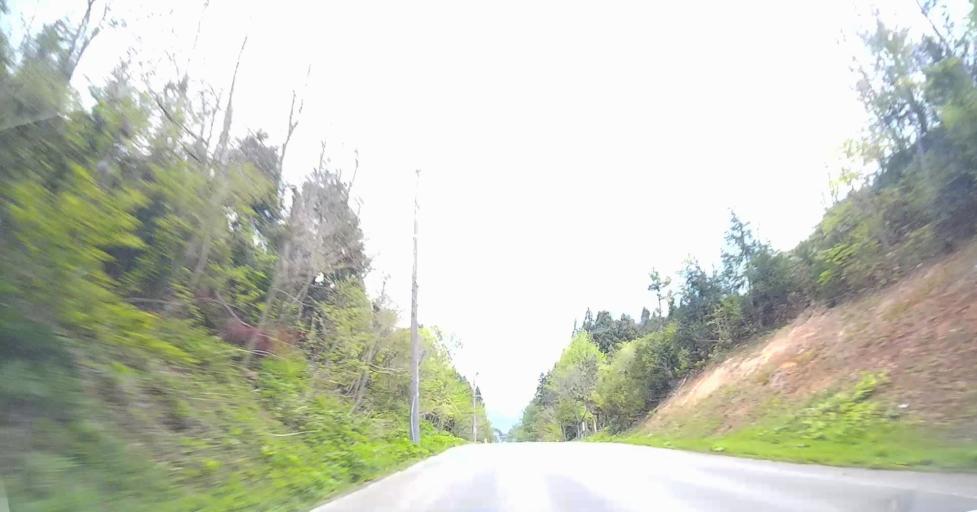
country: JP
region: Aomori
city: Shimokizukuri
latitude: 41.1784
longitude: 140.4727
